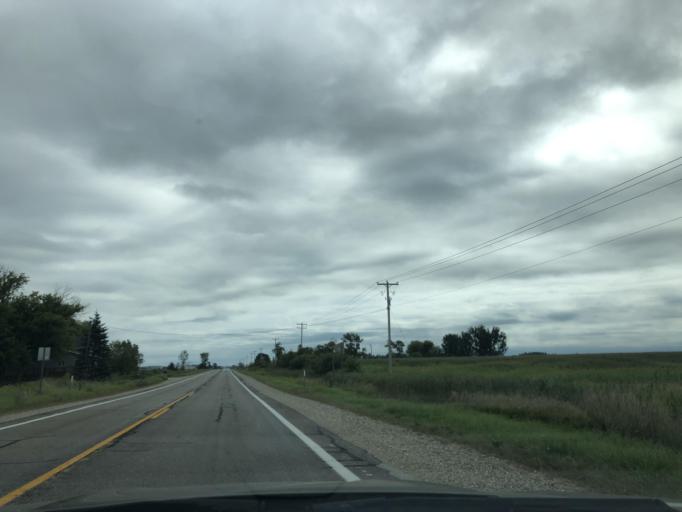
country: US
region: Michigan
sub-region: Missaukee County
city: Lake City
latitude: 44.1936
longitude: -85.1784
